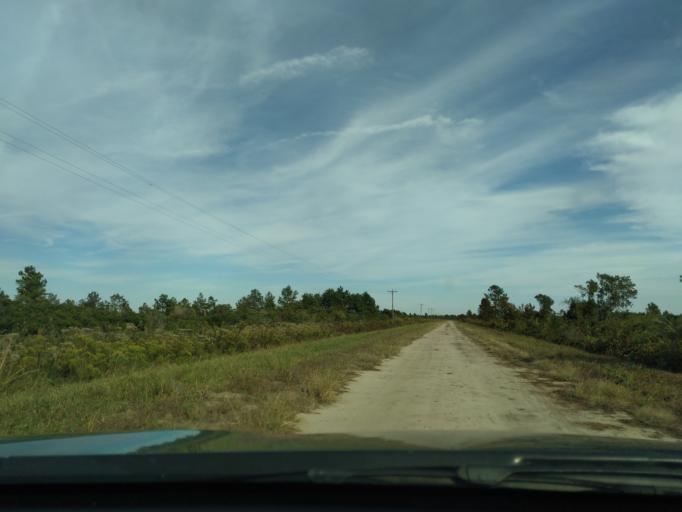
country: US
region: North Carolina
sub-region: Beaufort County
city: Belhaven
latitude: 35.6902
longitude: -76.5395
